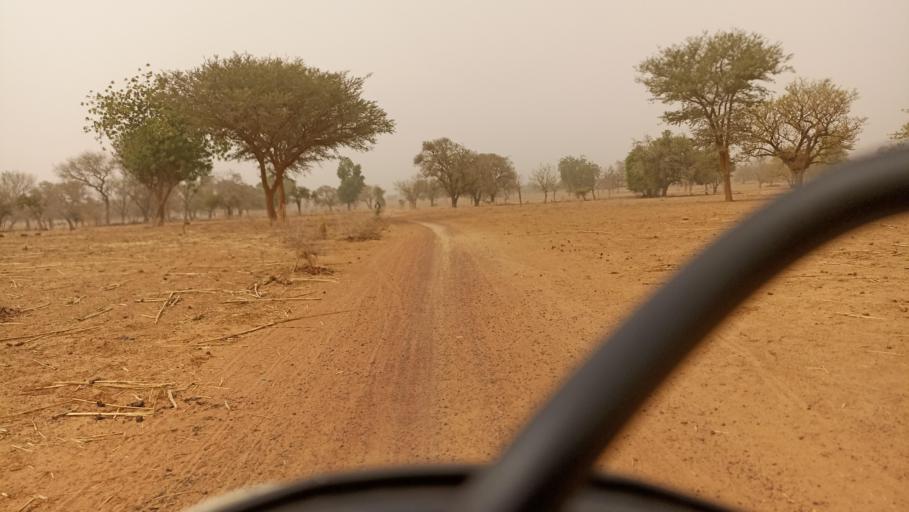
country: BF
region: Nord
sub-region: Province du Zondoma
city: Gourcy
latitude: 13.2739
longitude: -2.5374
